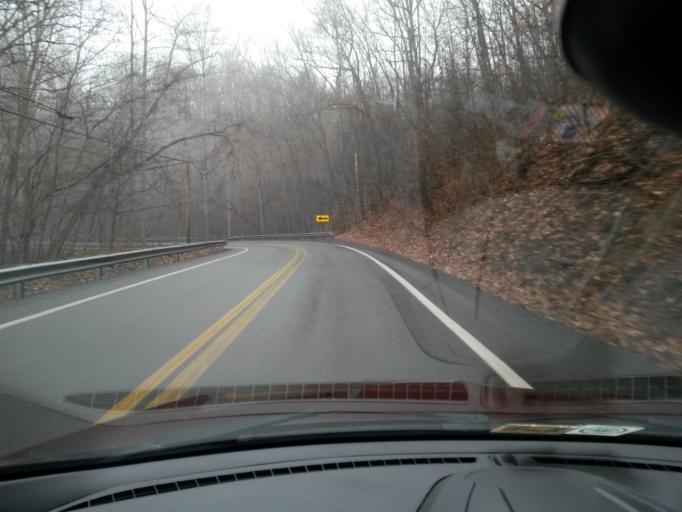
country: US
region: West Virginia
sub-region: Greenbrier County
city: Lewisburg
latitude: 37.8707
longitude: -80.5388
